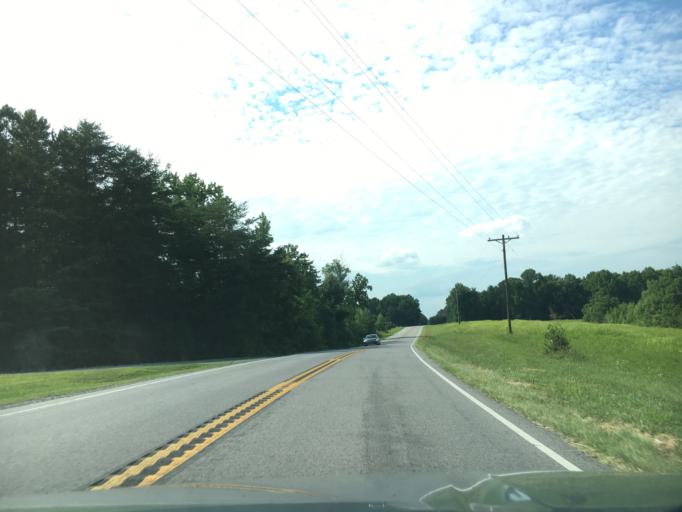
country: US
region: Virginia
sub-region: Halifax County
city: Mountain Road
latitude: 36.8562
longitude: -79.0053
